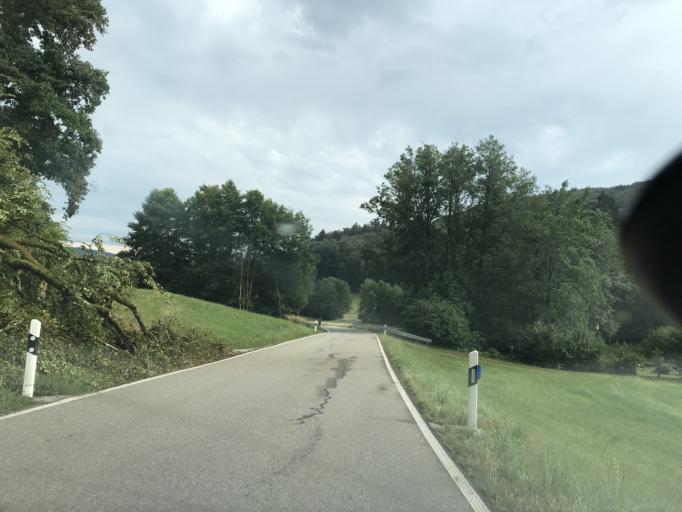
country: DE
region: Baden-Wuerttemberg
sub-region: Freiburg Region
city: Steinen
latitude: 47.6964
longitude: 7.7284
